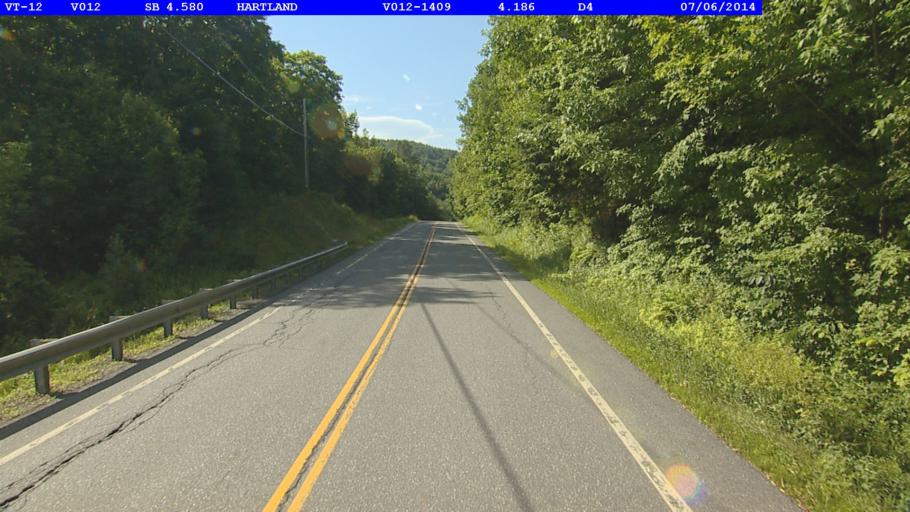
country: US
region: Vermont
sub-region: Windsor County
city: Woodstock
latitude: 43.5786
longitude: -72.4459
